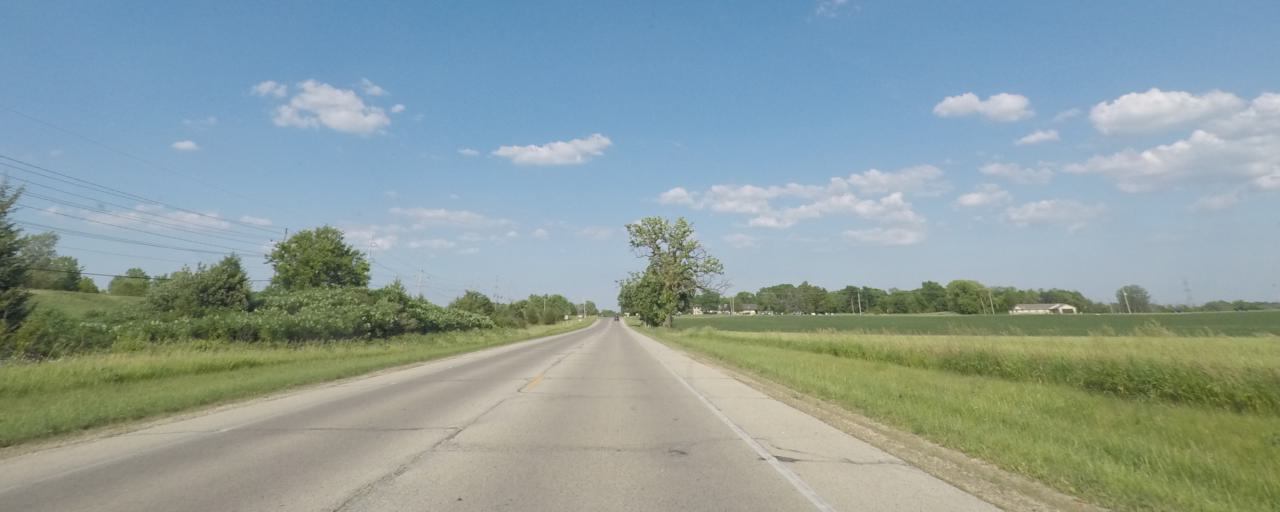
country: US
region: Wisconsin
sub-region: Waukesha County
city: Big Bend
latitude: 42.8875
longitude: -88.1898
